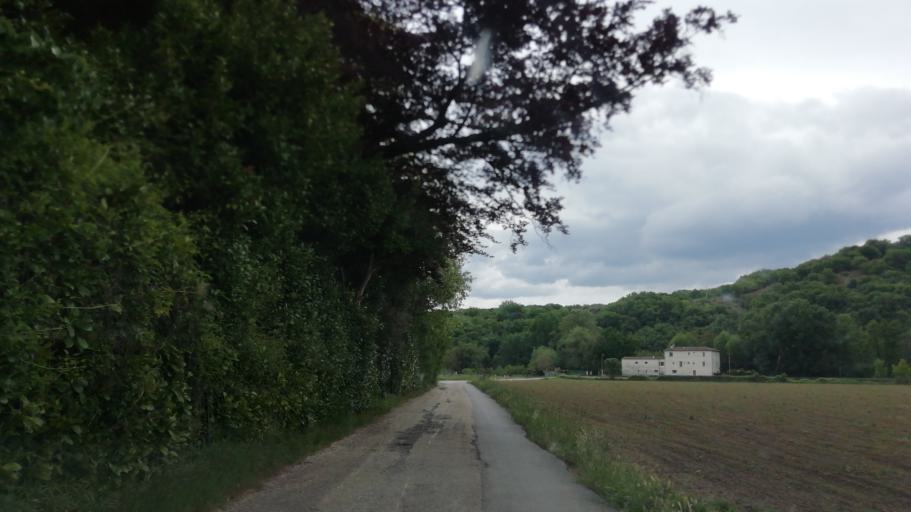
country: FR
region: Languedoc-Roussillon
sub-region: Departement de l'Herault
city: Cazilhac
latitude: 43.9223
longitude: 3.7128
